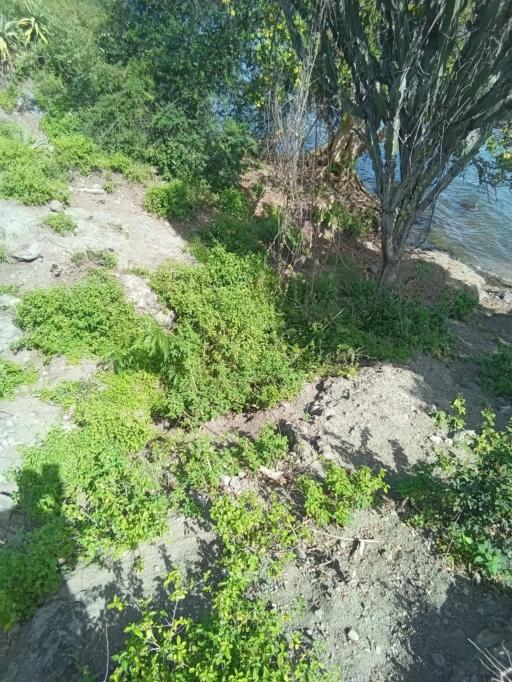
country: KE
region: Homa Bay
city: Homa Bay
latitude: -0.4806
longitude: 34.1677
